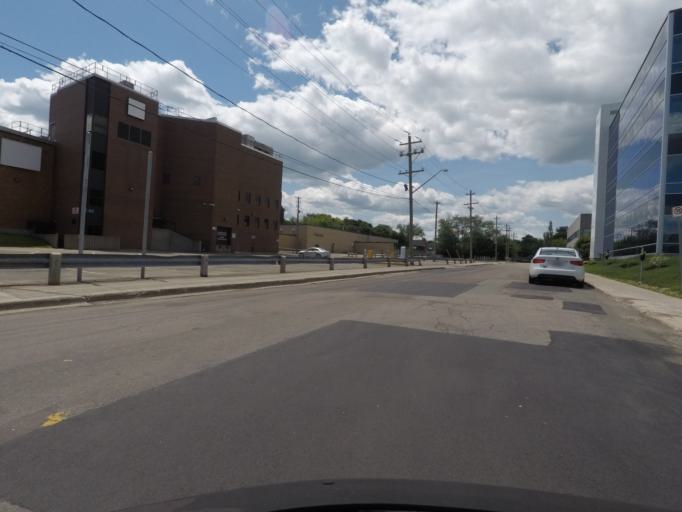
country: CA
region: New Brunswick
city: Moncton
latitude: 46.0969
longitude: -64.7856
